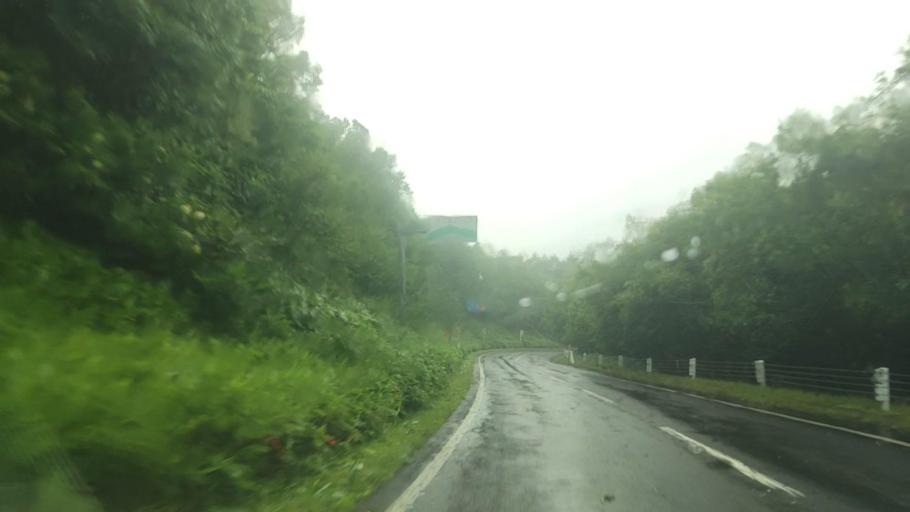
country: JP
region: Hokkaido
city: Shiraoi
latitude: 42.5423
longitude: 141.1065
